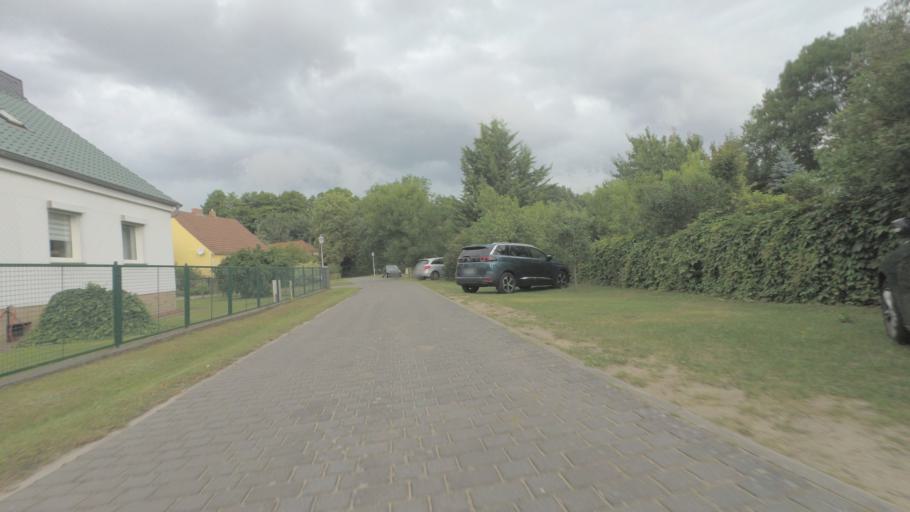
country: DE
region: Brandenburg
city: Bestensee
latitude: 52.2265
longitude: 13.6541
